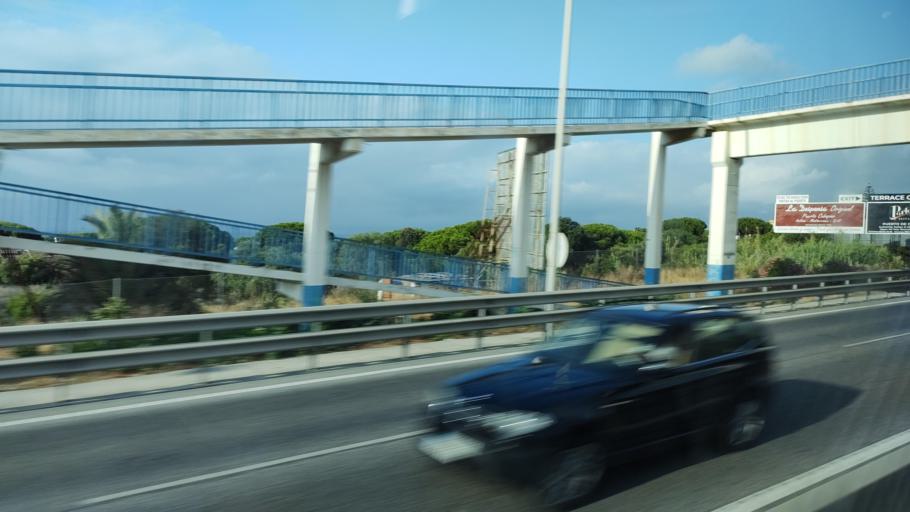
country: ES
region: Andalusia
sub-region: Provincia de Malaga
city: Fuengirola
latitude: 36.4879
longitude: -4.7376
